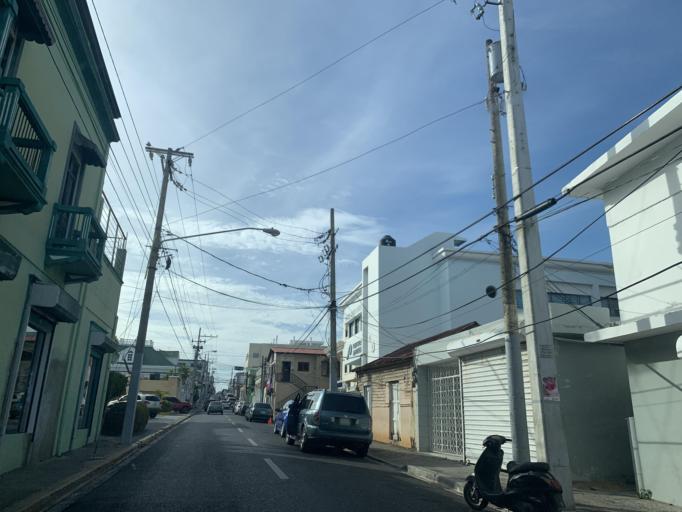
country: DO
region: Puerto Plata
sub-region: Puerto Plata
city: Puerto Plata
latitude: 19.7972
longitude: -70.6915
